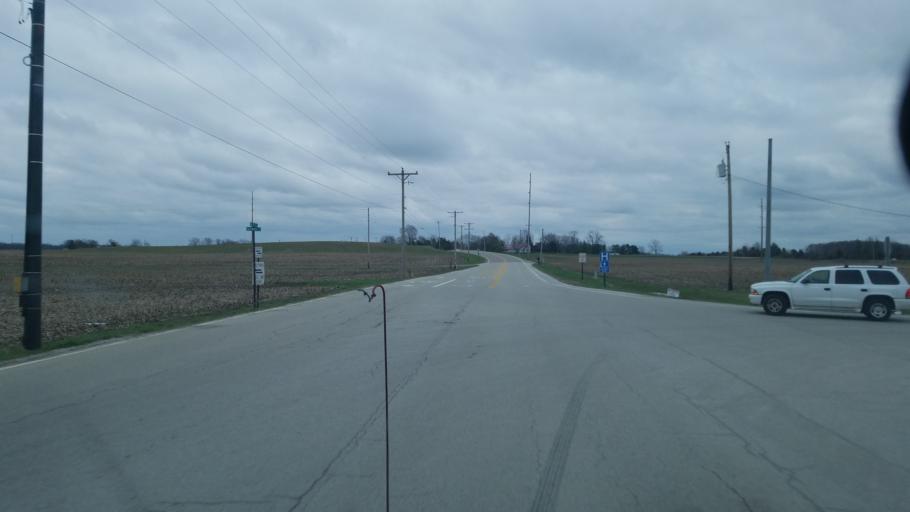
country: US
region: Ohio
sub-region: Fayette County
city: Washington Court House
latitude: 39.5517
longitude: -83.4859
